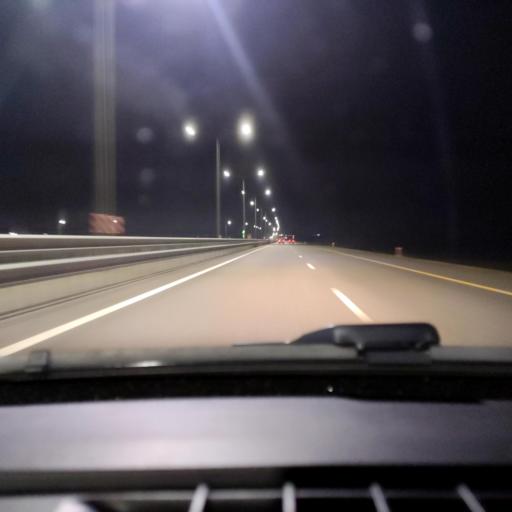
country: RU
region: Voronezj
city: Podkletnoye
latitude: 51.5555
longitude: 39.4869
